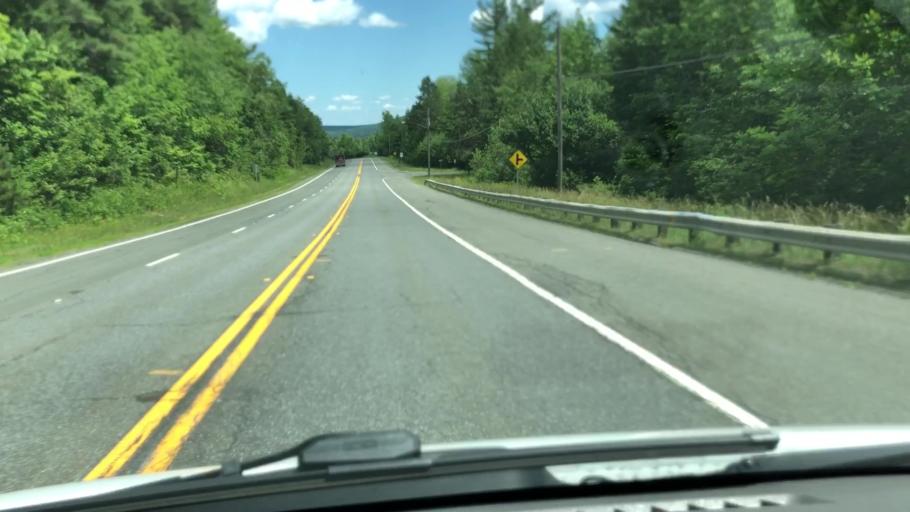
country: US
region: Massachusetts
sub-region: Berkshire County
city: Hinsdale
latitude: 42.4982
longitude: -73.0270
